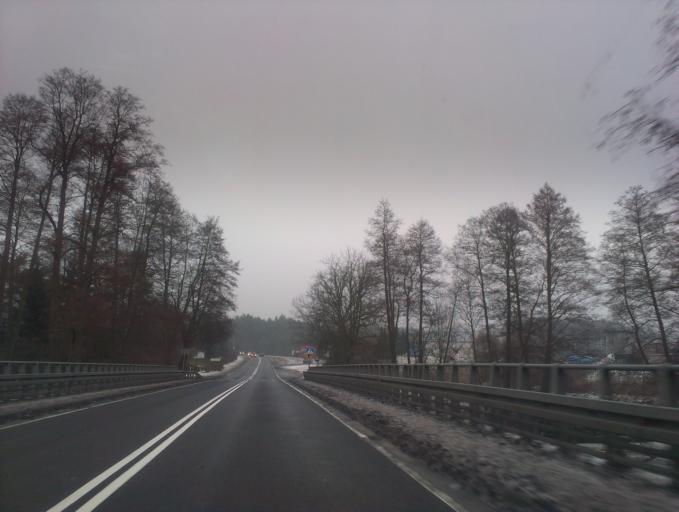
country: PL
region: Greater Poland Voivodeship
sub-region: Powiat pilski
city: Pila
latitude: 53.2198
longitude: 16.7870
